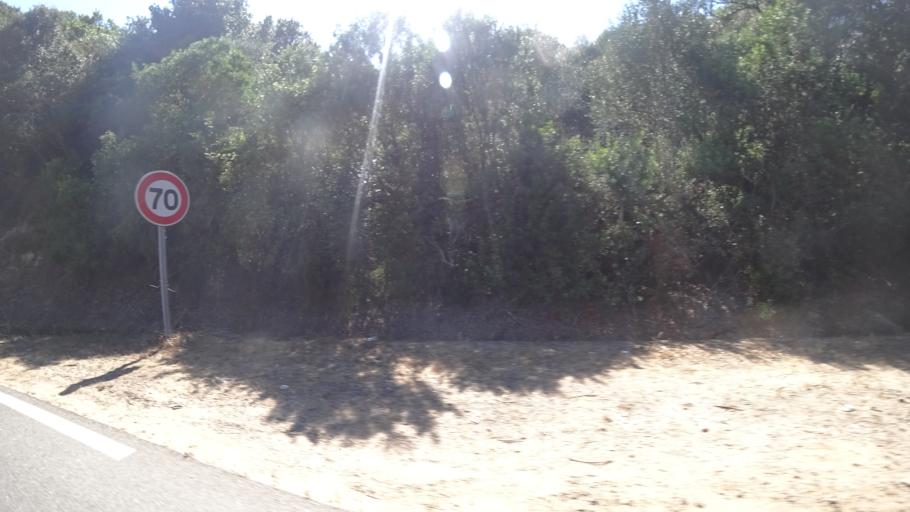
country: FR
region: Corsica
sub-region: Departement de la Corse-du-Sud
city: Alata
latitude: 41.9599
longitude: 8.7256
